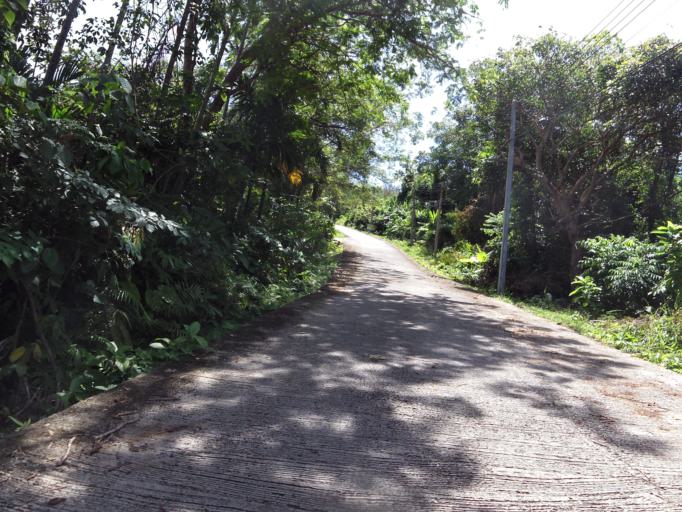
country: TH
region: Phuket
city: Ban Karon
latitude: 7.8470
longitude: 98.3049
